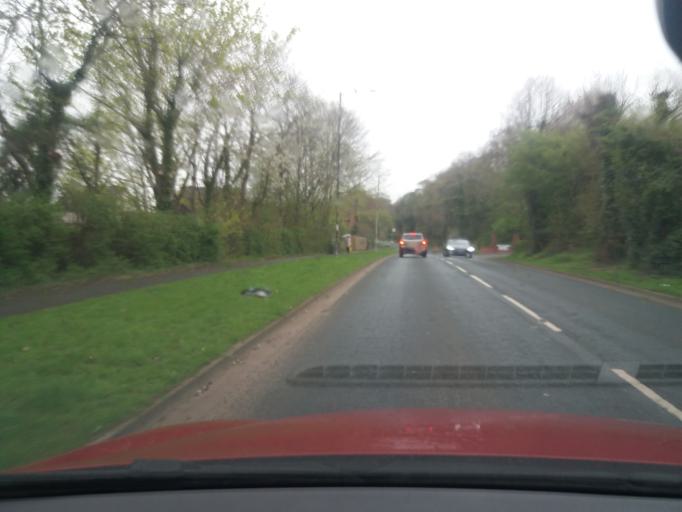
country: GB
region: England
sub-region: Lancashire
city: Clayton-le-Woods
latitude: 53.6974
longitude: -2.6342
